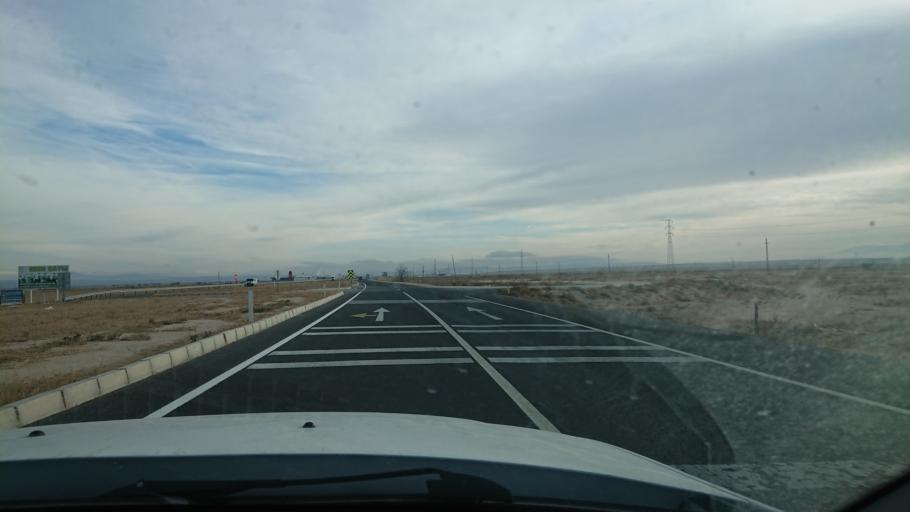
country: TR
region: Aksaray
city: Yesilova
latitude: 38.3103
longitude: 33.8316
